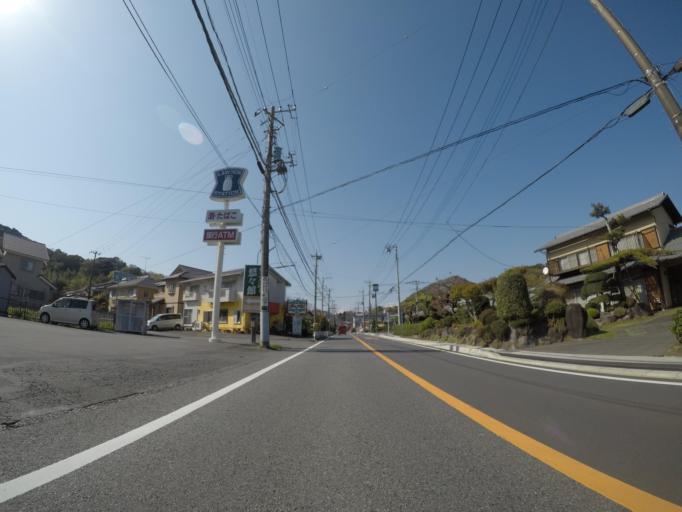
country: JP
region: Shizuoka
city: Mishima
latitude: 35.0367
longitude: 138.9270
